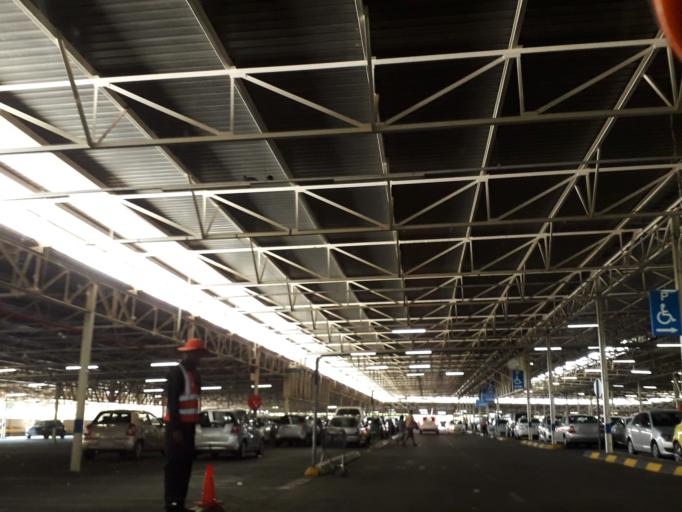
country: ZA
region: Gauteng
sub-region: City of Johannesburg Metropolitan Municipality
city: Johannesburg
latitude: -26.1469
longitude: 28.0794
